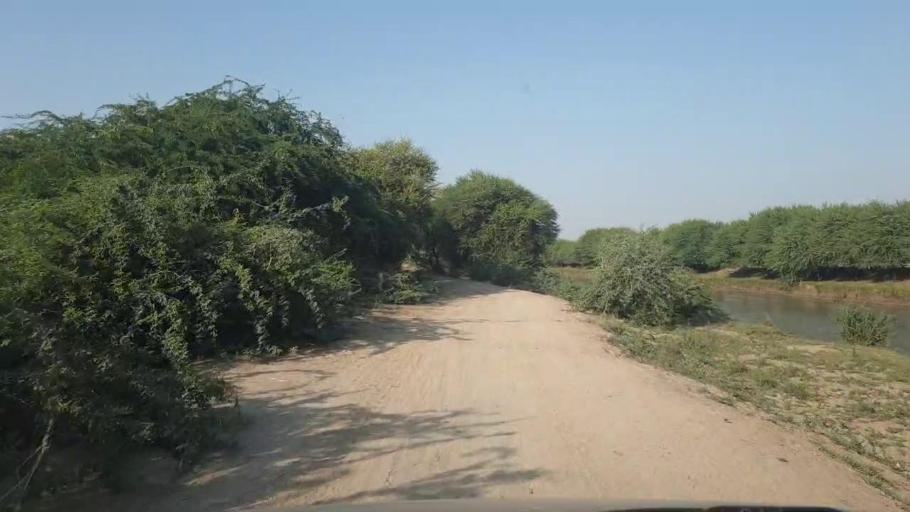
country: PK
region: Sindh
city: Badin
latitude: 24.6405
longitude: 68.8150
